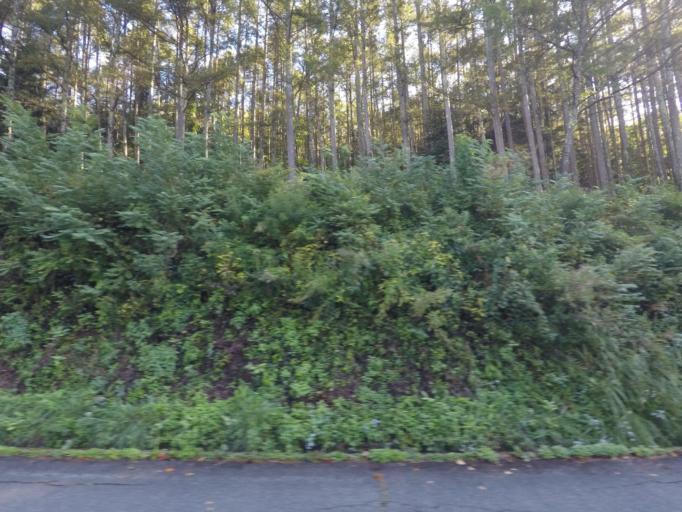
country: JP
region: Nagano
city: Ina
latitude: 35.9543
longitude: 137.7792
